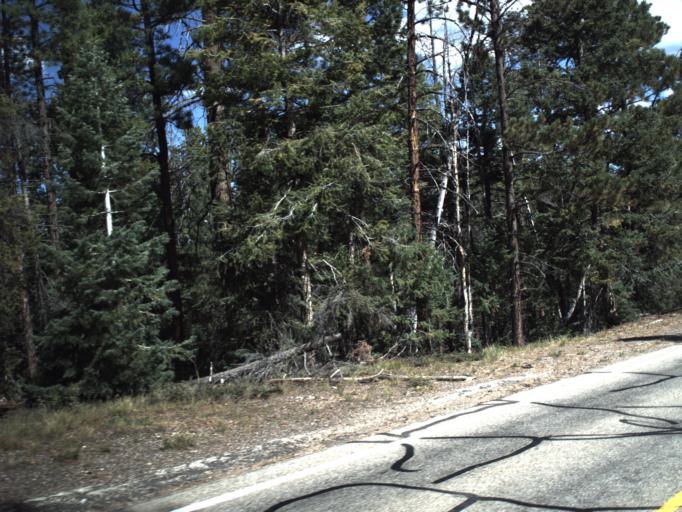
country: US
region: Utah
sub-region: Garfield County
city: Panguitch
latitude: 37.5138
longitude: -112.6365
